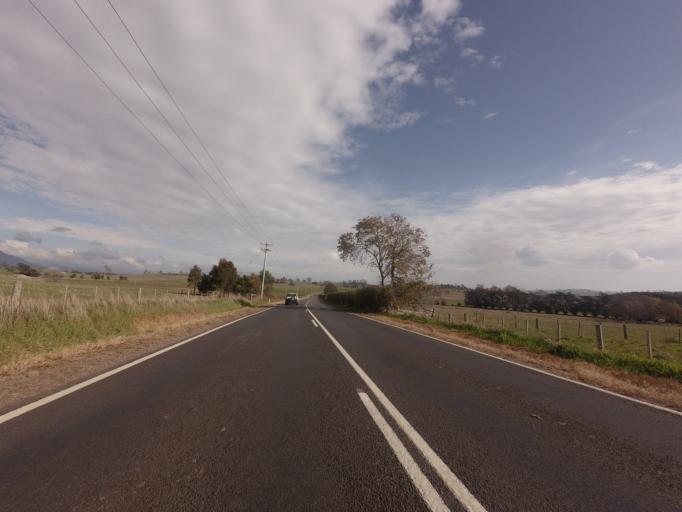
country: AU
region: Tasmania
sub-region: Meander Valley
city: Deloraine
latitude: -41.5225
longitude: 146.7182
